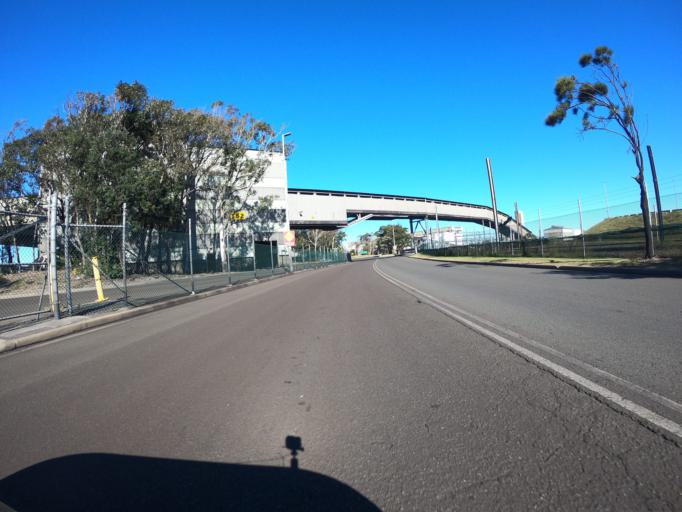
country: AU
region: New South Wales
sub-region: Wollongong
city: Coniston
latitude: -34.4466
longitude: 150.8982
